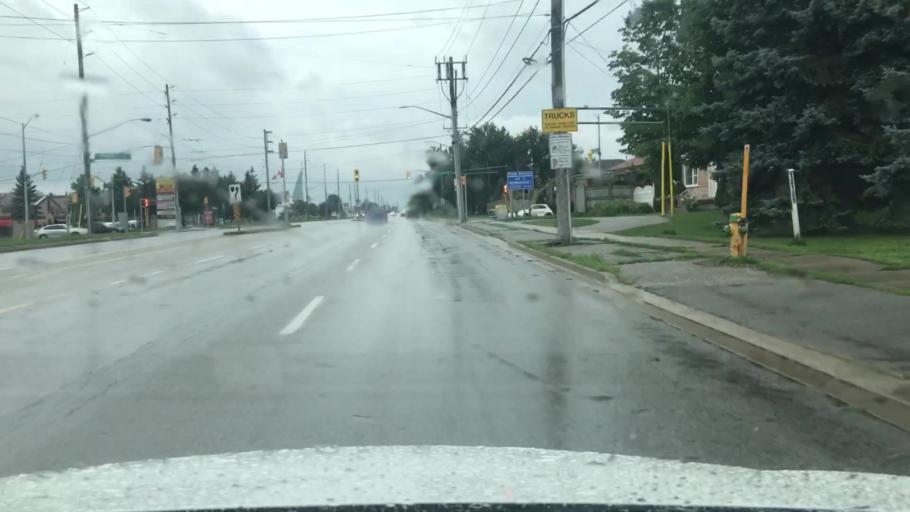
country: CA
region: Ontario
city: Newmarket
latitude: 44.0809
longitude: -79.4358
